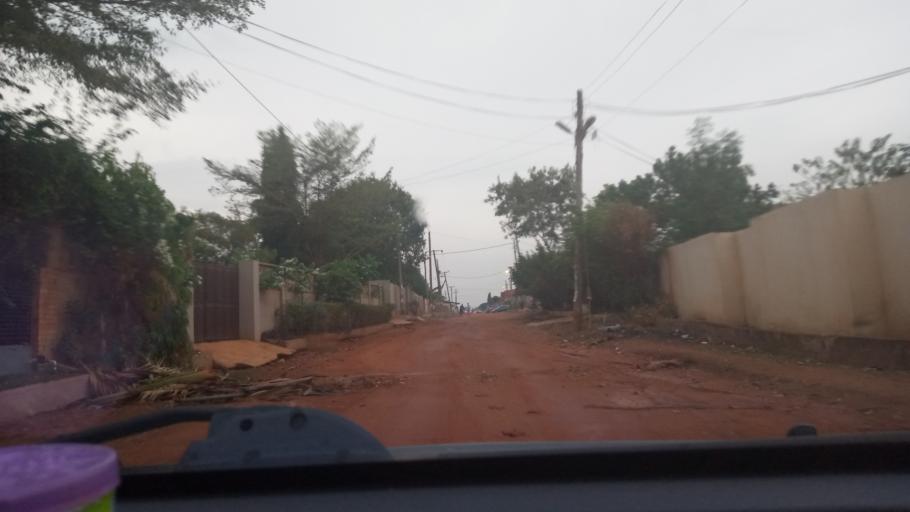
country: GH
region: Greater Accra
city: Medina Estates
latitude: 5.7038
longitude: -0.1671
